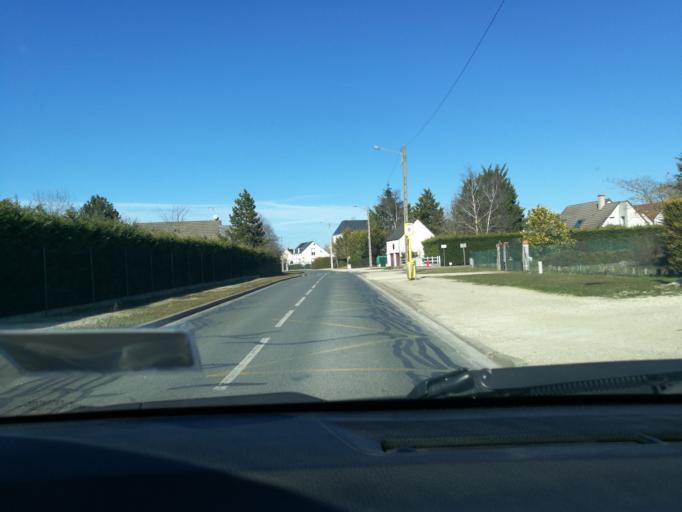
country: FR
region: Centre
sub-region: Departement du Loiret
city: Saint-Jean-le-Blanc
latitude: 47.8731
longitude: 1.9270
